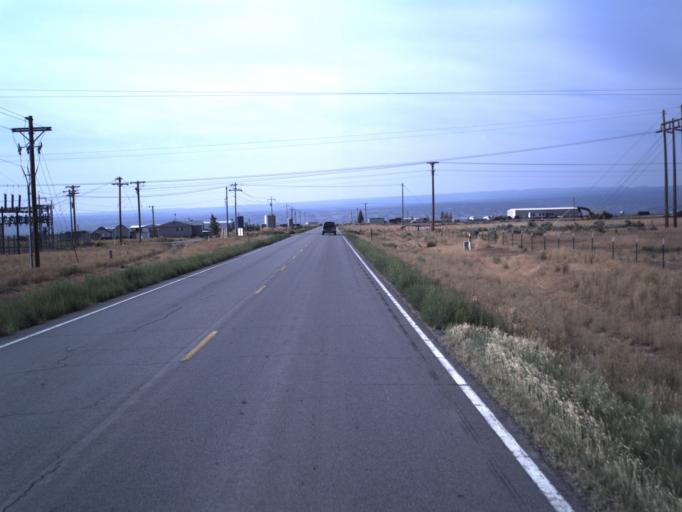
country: US
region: Utah
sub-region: Duchesne County
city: Duchesne
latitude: 40.2145
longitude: -110.3893
